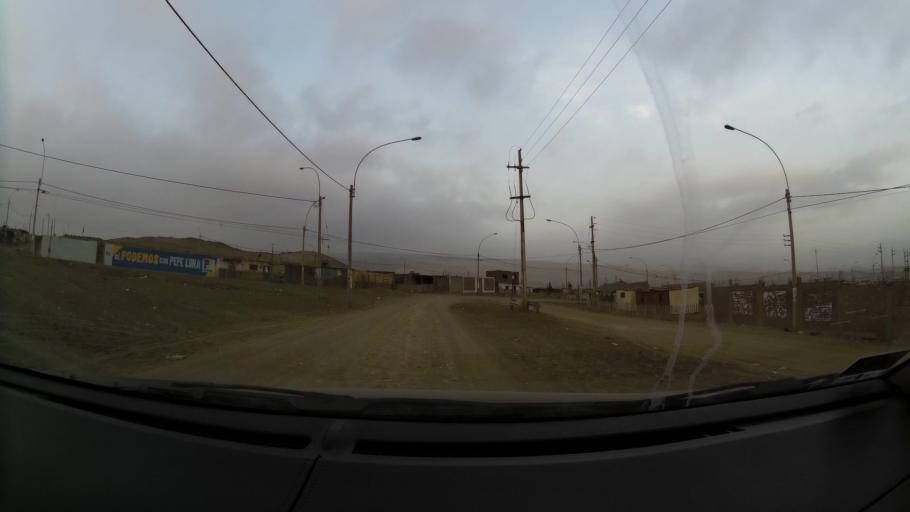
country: PE
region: Lima
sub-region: Lima
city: Santa Rosa
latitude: -11.7306
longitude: -77.1396
